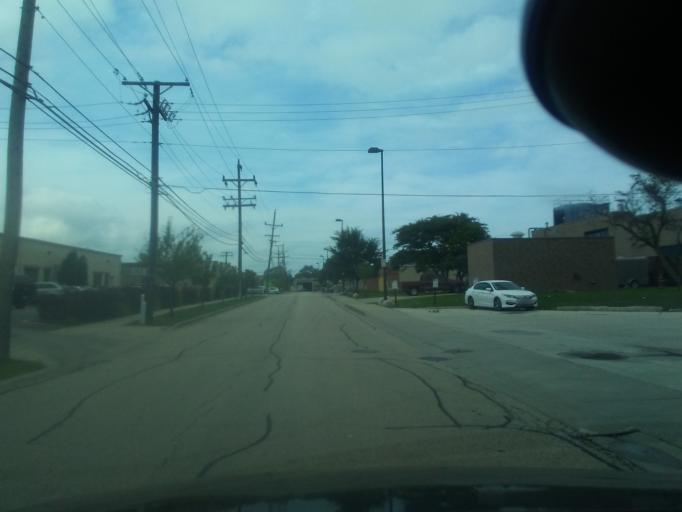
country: US
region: Illinois
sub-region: Cook County
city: Skokie
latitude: 42.0277
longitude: -87.7157
